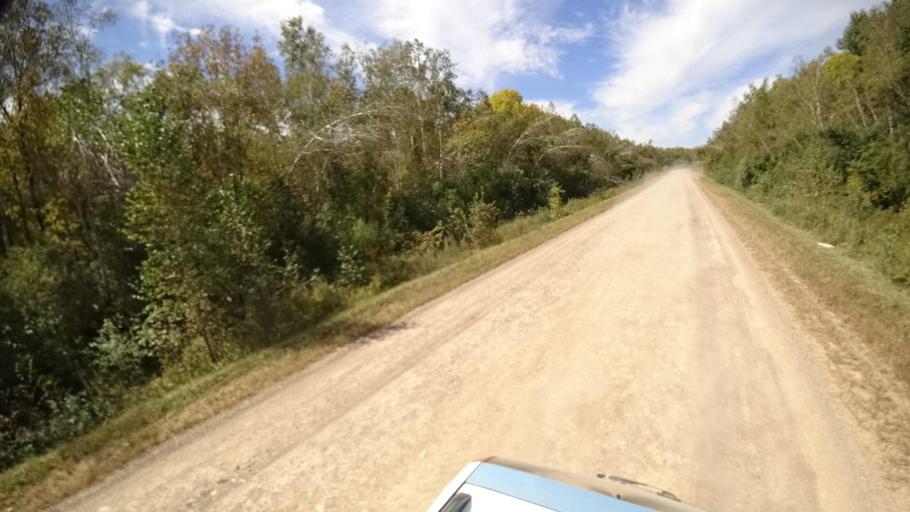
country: RU
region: Primorskiy
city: Yakovlevka
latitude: 44.6592
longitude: 133.7312
